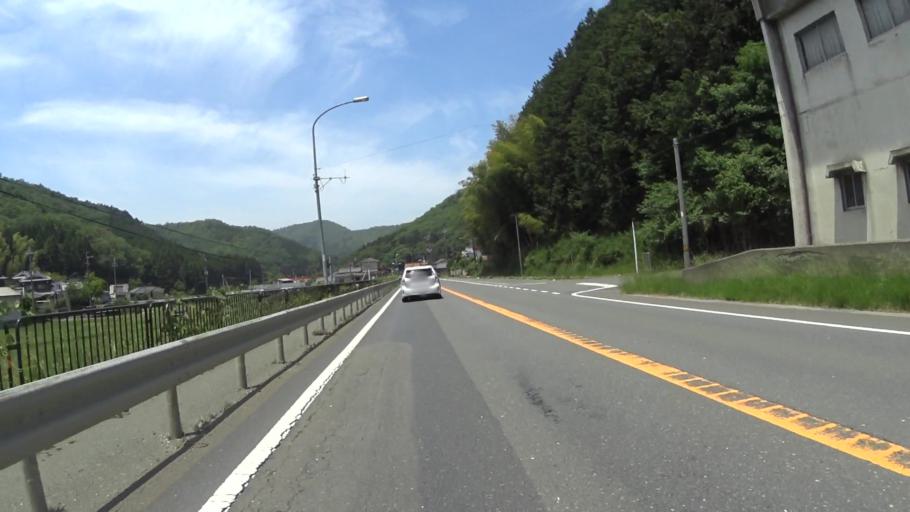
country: JP
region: Kyoto
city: Kameoka
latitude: 35.1322
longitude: 135.4307
